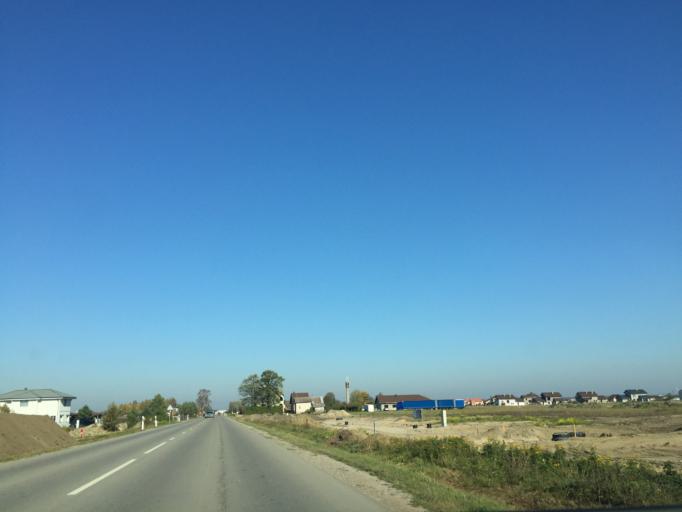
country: LT
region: Klaipedos apskritis
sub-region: Klaipeda
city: Klaipeda
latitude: 55.7484
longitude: 21.1924
